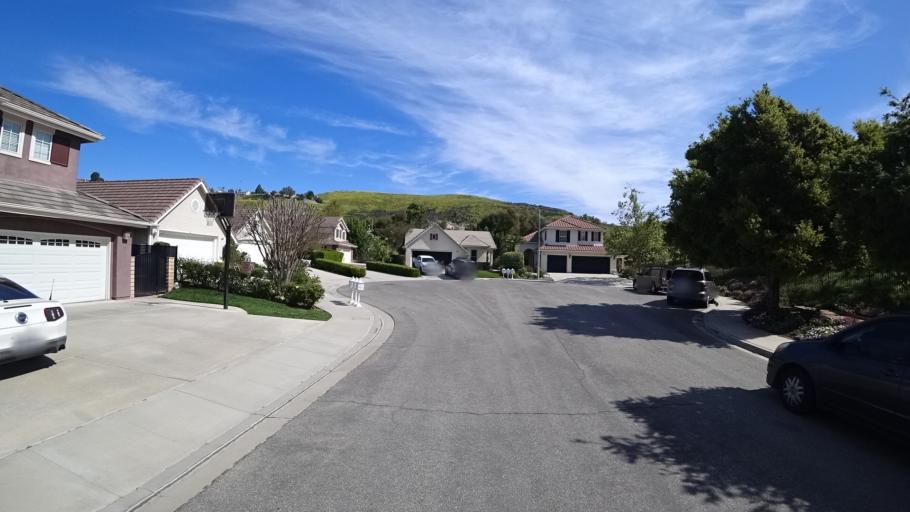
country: US
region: California
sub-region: Ventura County
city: Thousand Oaks
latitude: 34.2217
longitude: -118.8305
